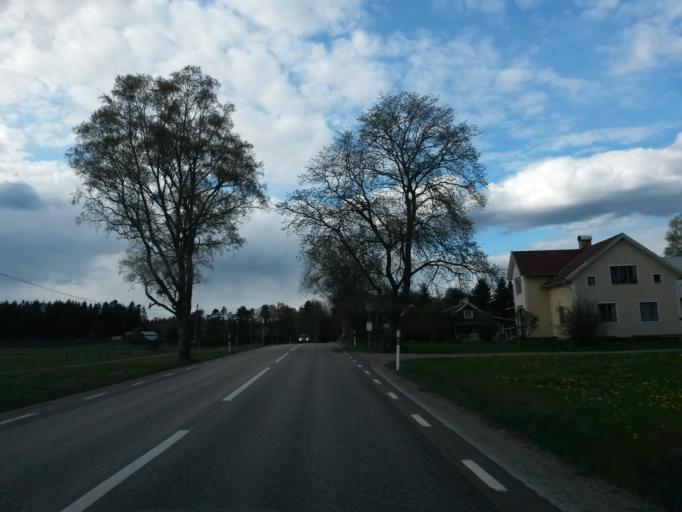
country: SE
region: Vaestra Goetaland
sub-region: Svenljunga Kommun
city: Svenljunga
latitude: 57.5882
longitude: 13.1236
